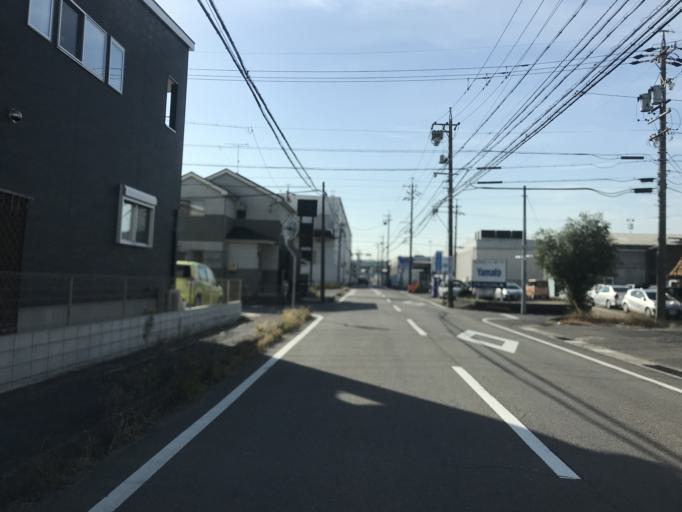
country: JP
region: Aichi
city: Iwakura
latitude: 35.2291
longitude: 136.8544
